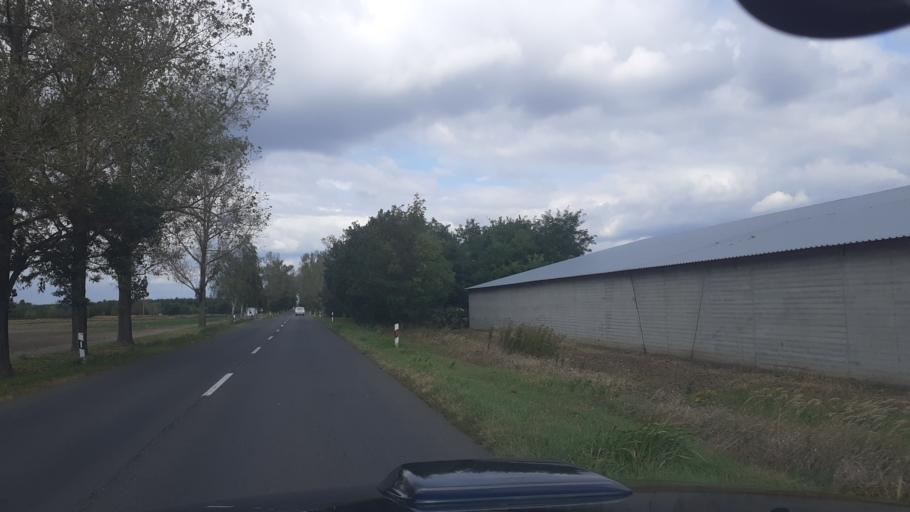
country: HU
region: Bacs-Kiskun
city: Apostag
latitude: 46.8900
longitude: 18.9770
